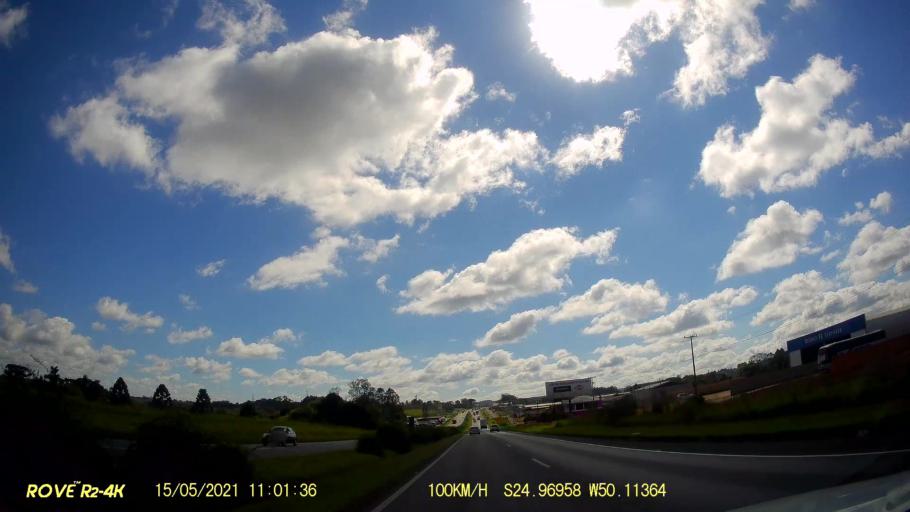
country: BR
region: Parana
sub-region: Carambei
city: Carambei
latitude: -24.9697
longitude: -50.1136
